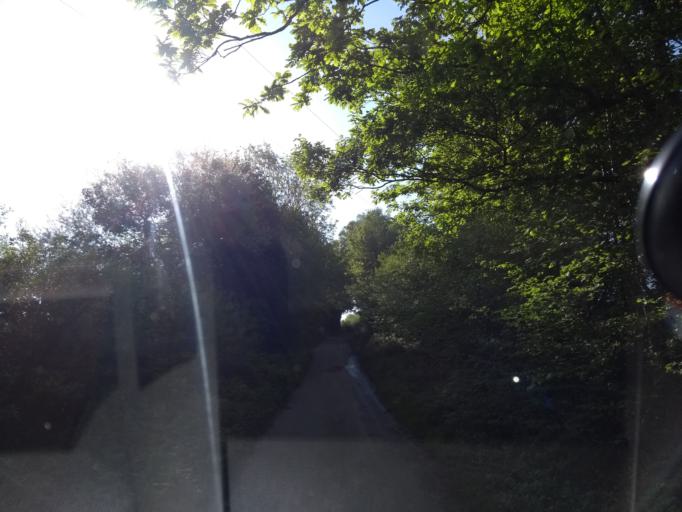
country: GB
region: England
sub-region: Dorset
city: Lyme Regis
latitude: 50.7940
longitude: -2.8893
